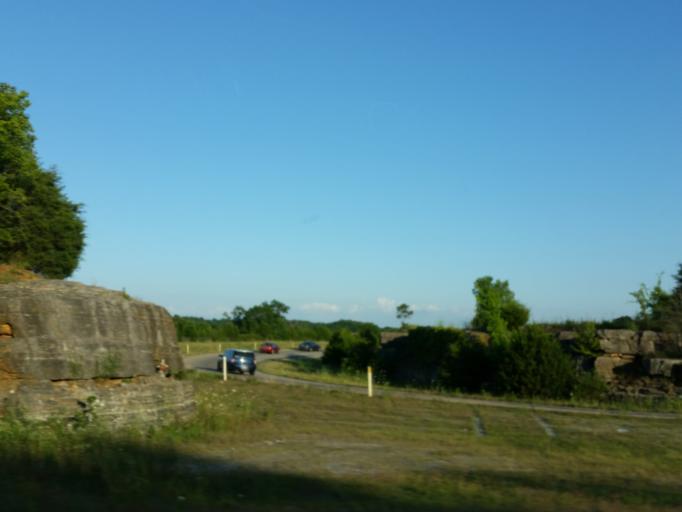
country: US
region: Tennessee
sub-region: Wilson County
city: Rural Hill
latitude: 36.1311
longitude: -86.3960
